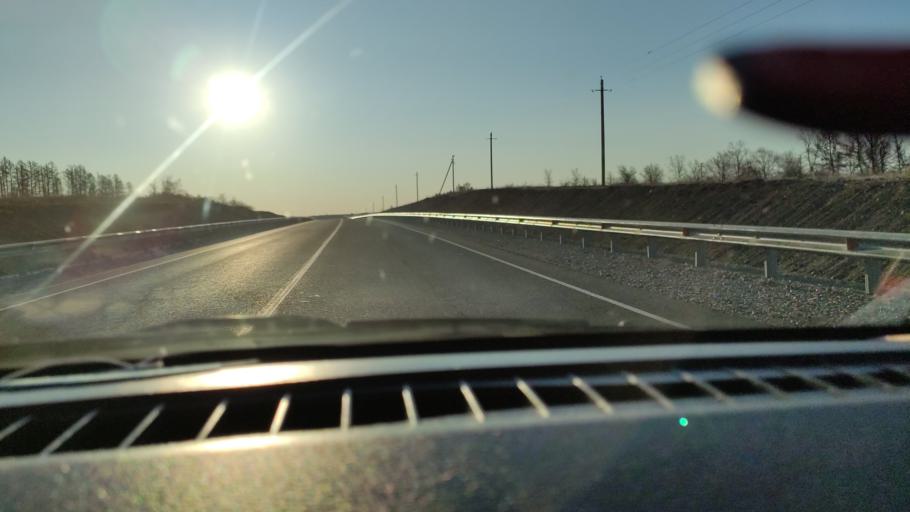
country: RU
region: Saratov
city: Shikhany
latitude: 52.1610
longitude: 47.1137
